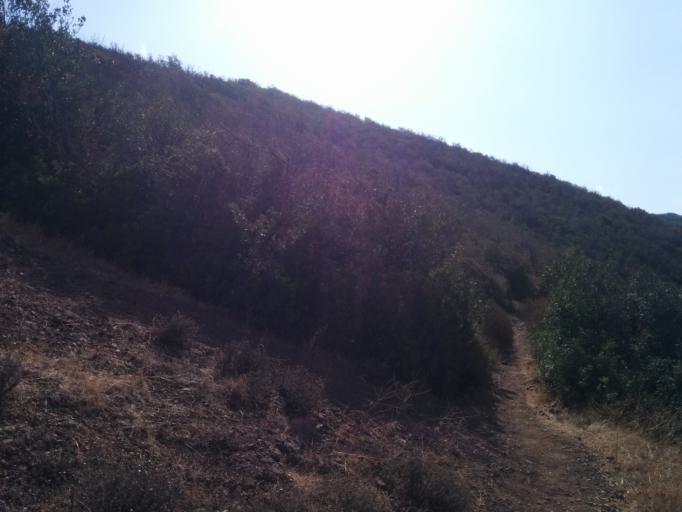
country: IT
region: Tuscany
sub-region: Provincia di Livorno
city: Portoferraio
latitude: 42.7542
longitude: 10.3142
